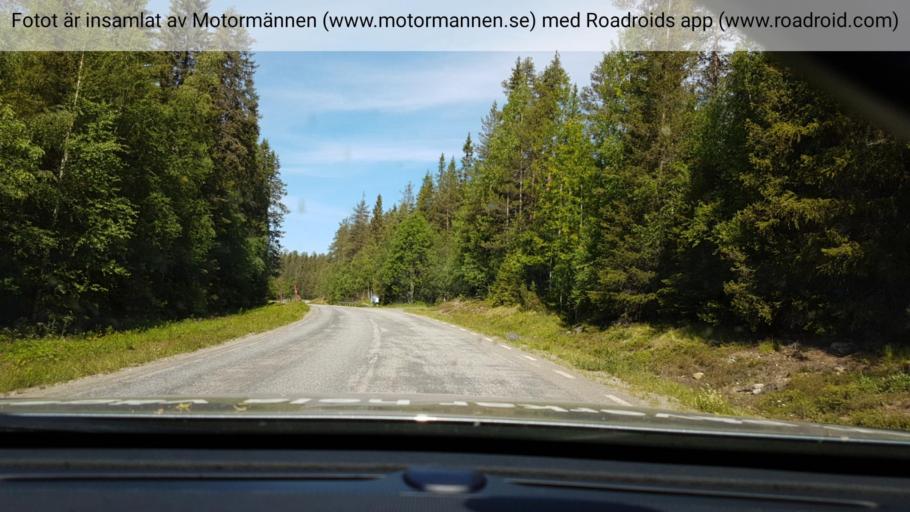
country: SE
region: Vaesterbotten
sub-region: Vilhelmina Kommun
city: Sjoberg
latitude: 64.6257
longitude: 15.8317
